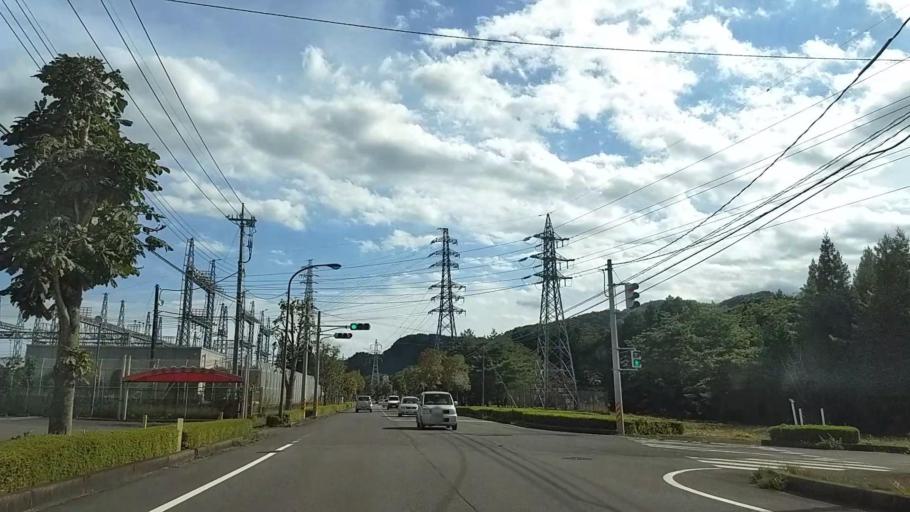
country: JP
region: Tochigi
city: Imaichi
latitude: 36.7868
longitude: 139.7024
